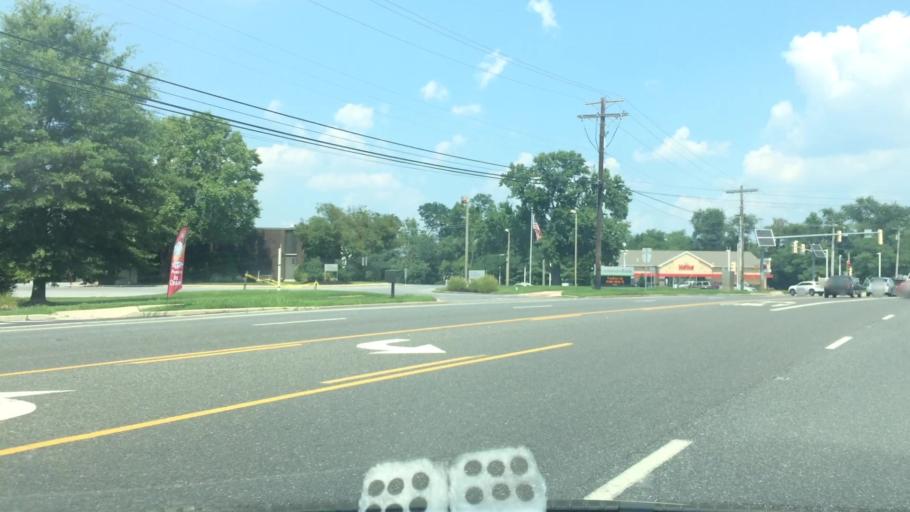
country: US
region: New Jersey
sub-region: Gloucester County
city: Turnersville
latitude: 39.7503
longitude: -75.0772
